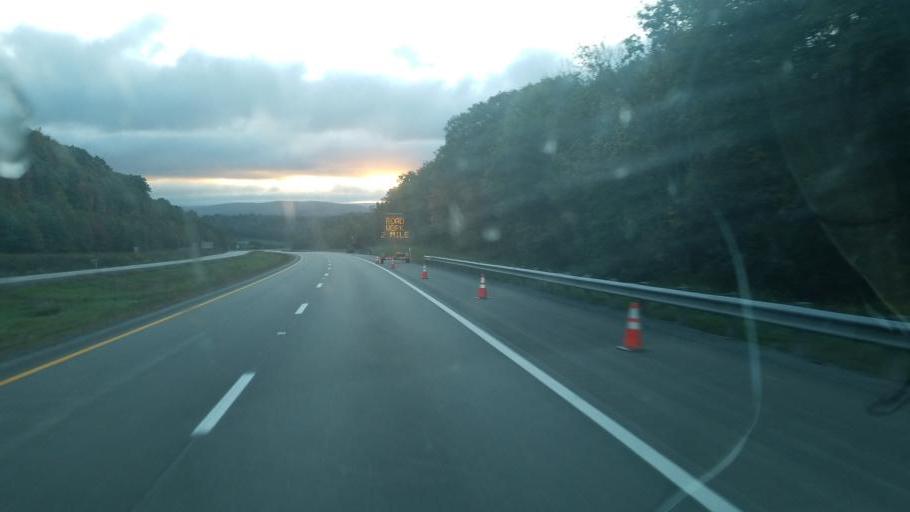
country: US
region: West Virginia
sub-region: Preston County
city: Terra Alta
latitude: 39.6629
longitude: -79.4841
